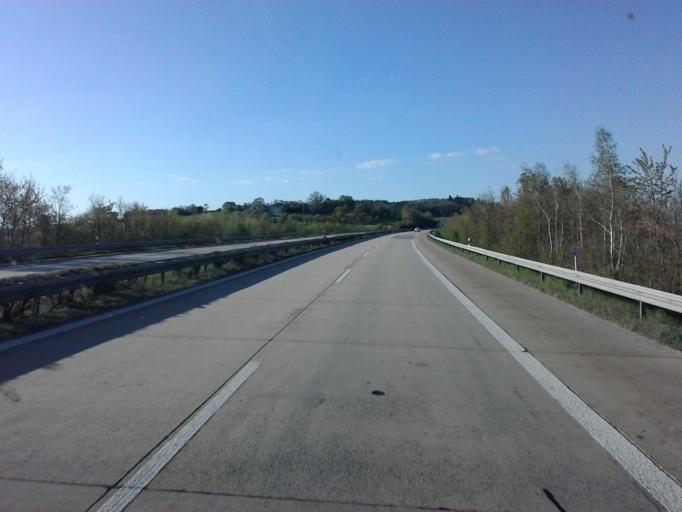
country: DE
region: Bavaria
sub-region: Regierungsbezirk Mittelfranken
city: Schnelldorf
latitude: 49.2325
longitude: 10.2125
